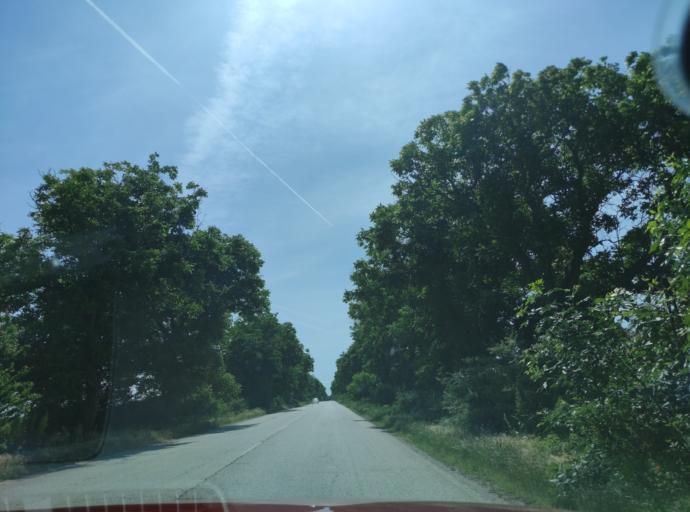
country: BG
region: Pleven
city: Iskur
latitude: 43.4444
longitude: 24.3341
